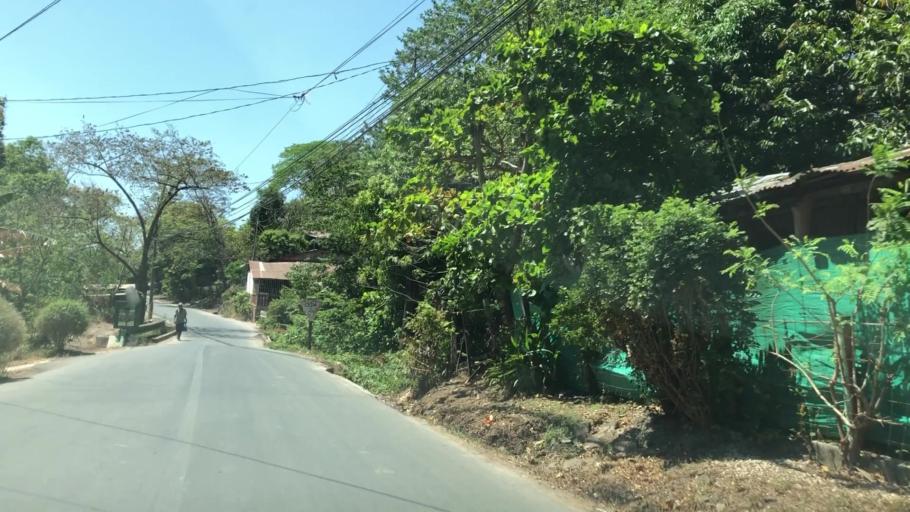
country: CR
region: Guanacaste
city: Sardinal
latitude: 10.3606
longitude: -85.8108
